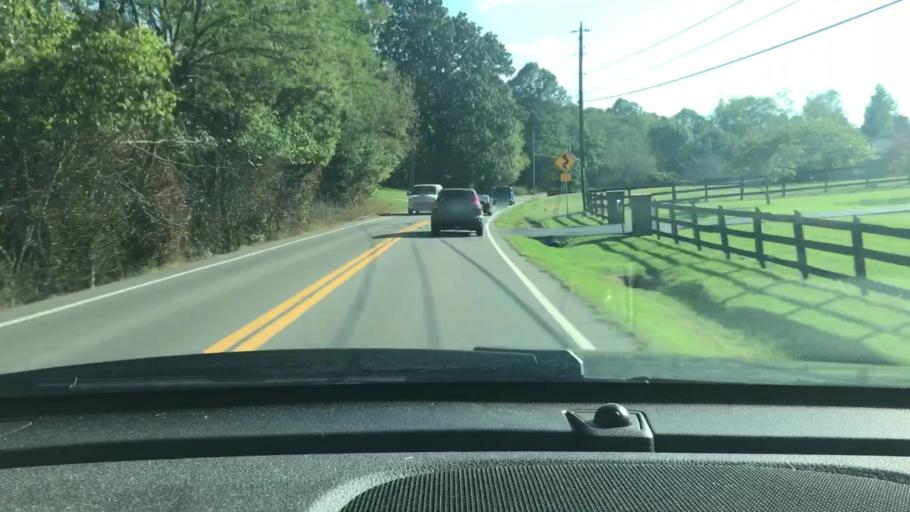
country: US
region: Tennessee
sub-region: Sumner County
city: White House
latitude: 36.4393
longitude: -86.6457
